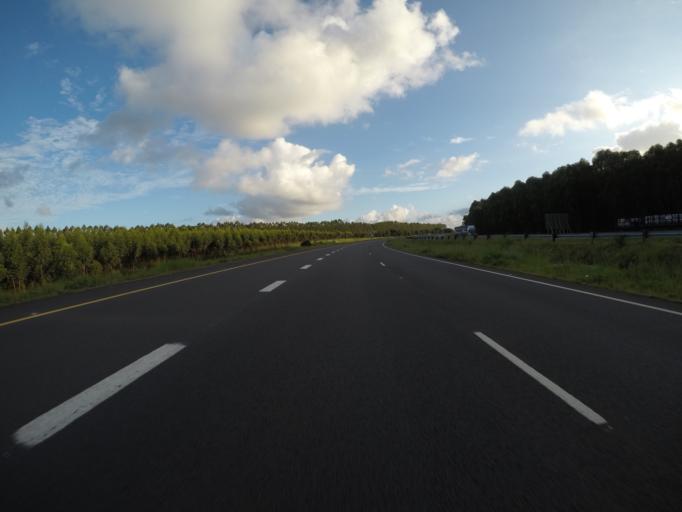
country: ZA
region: KwaZulu-Natal
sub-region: uThungulu District Municipality
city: KwaMbonambi
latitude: -28.5251
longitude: 32.1382
